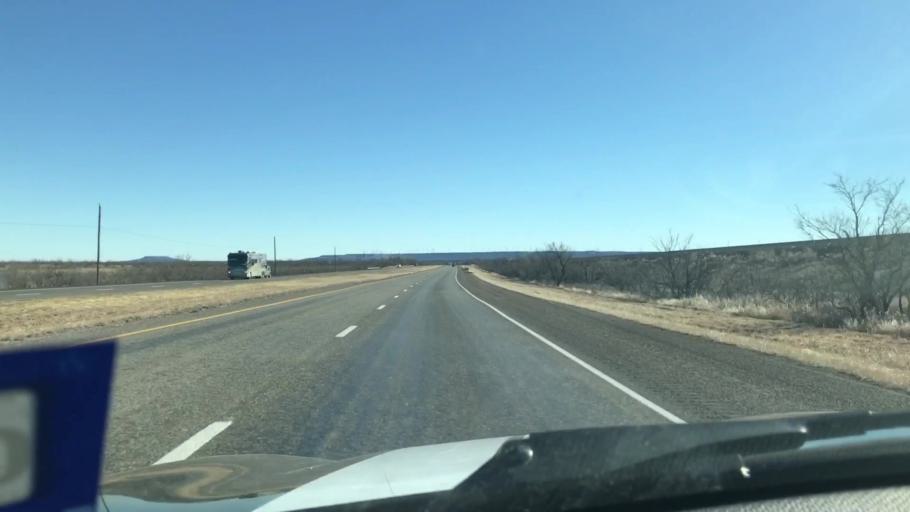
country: US
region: Texas
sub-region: Garza County
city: Post
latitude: 33.0576
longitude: -101.2155
